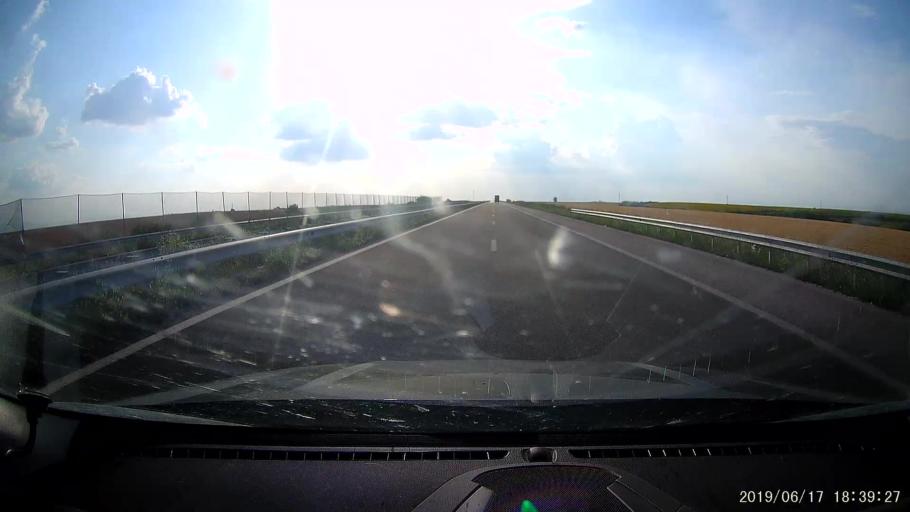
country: BG
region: Stara Zagora
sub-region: Obshtina Chirpan
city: Chirpan
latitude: 42.1453
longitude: 25.3069
